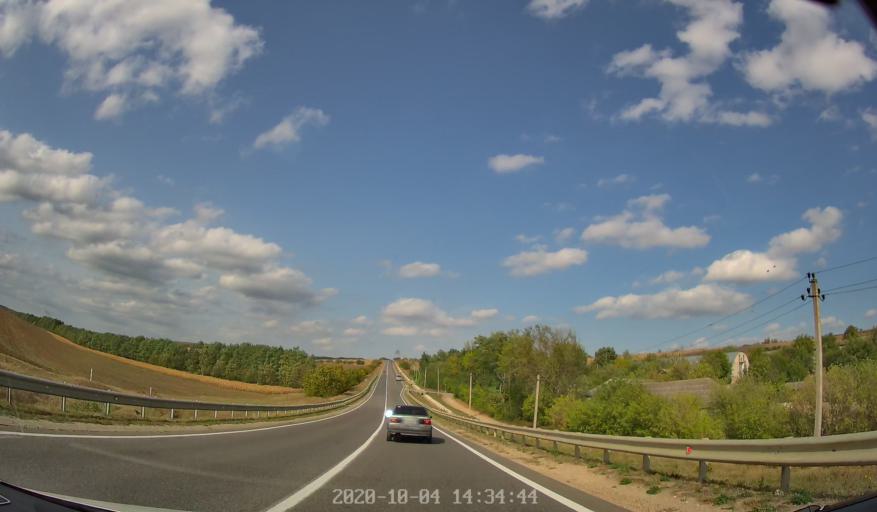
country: MD
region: Soldanesti
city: Soldanesti
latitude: 47.7054
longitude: 28.8470
